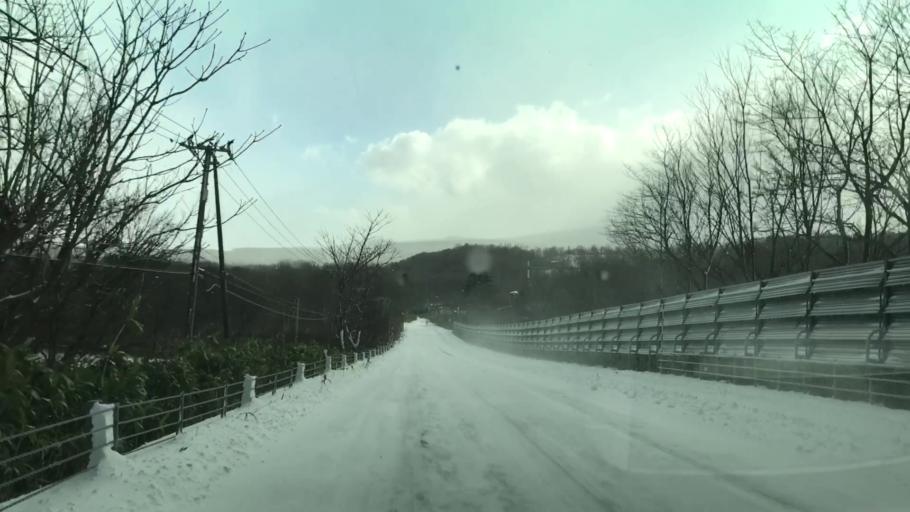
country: JP
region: Hokkaido
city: Yoichi
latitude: 43.3337
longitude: 140.4665
